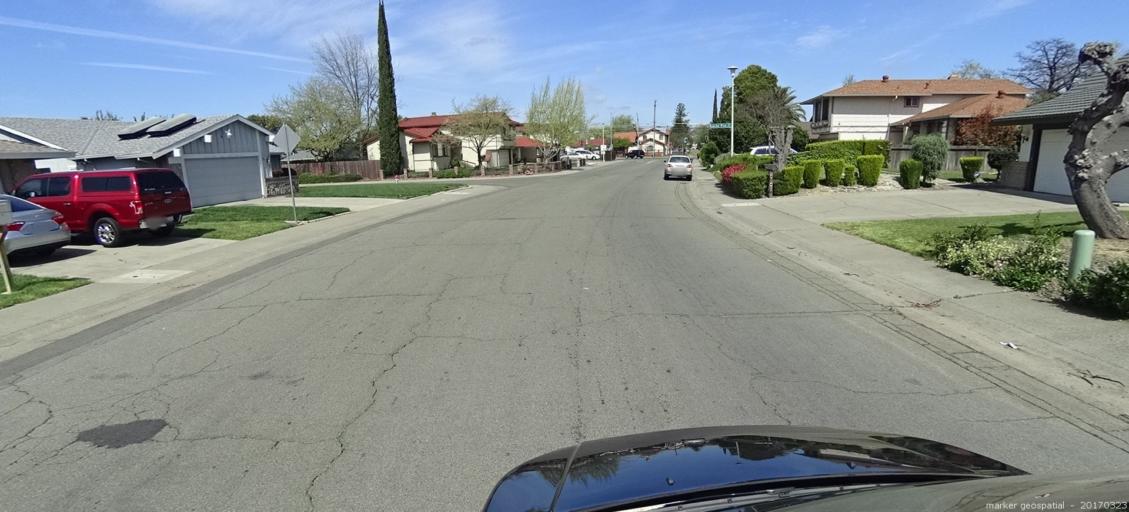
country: US
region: California
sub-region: Sacramento County
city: Florin
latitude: 38.5094
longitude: -121.4224
